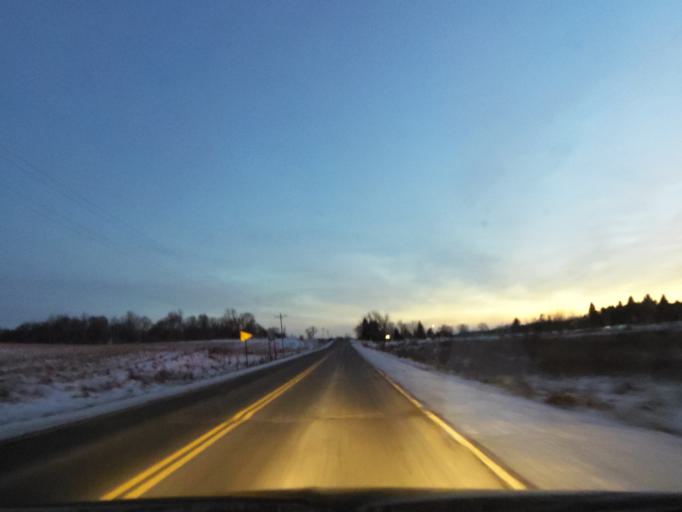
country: US
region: Minnesota
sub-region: Chisago County
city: Center City
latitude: 45.3810
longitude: -92.7952
